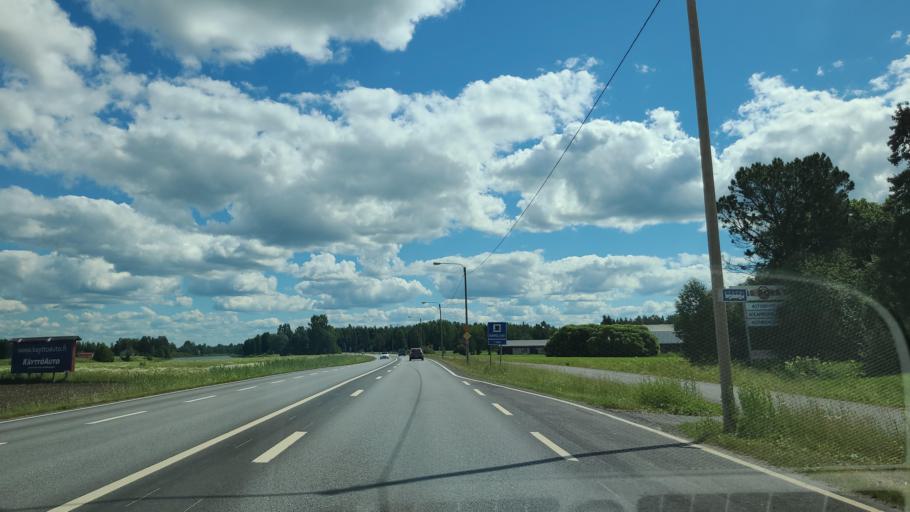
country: FI
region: Ostrobothnia
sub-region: Kyroenmaa
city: Isokyroe
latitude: 62.9760
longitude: 22.3619
